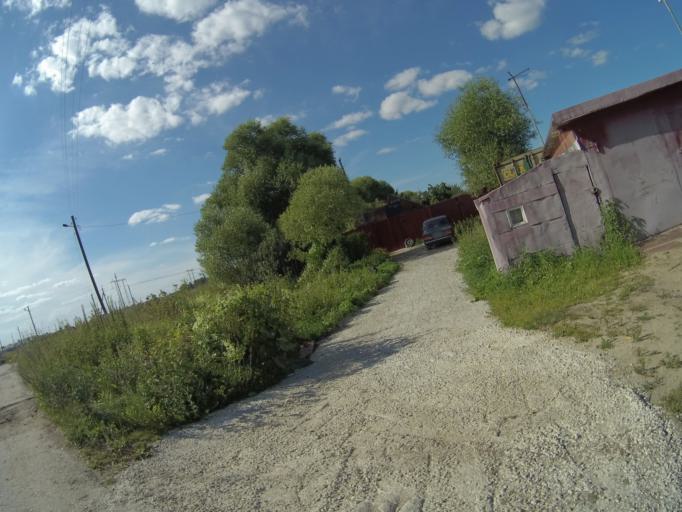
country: RU
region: Vladimir
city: Vorsha
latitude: 56.0953
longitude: 40.1899
